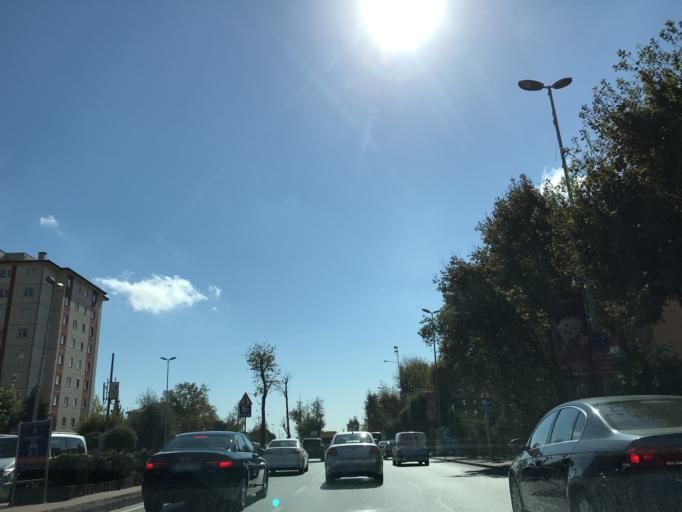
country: TR
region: Istanbul
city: Sisli
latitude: 41.0570
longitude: 29.0098
